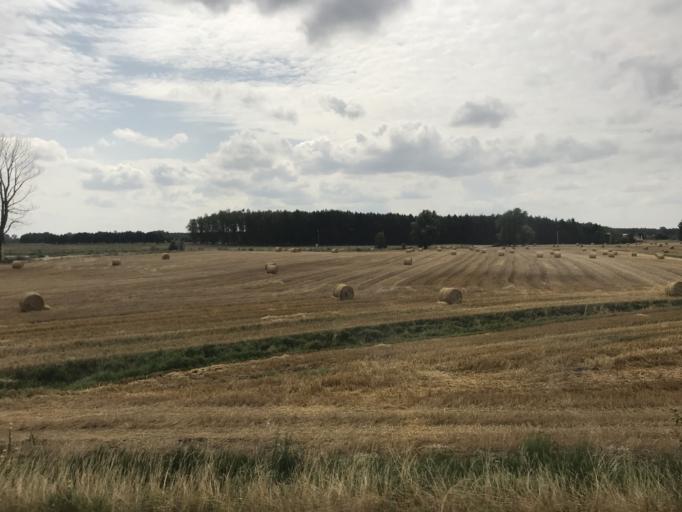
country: PL
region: Greater Poland Voivodeship
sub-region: Powiat gnieznienski
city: Trzemeszno
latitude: 52.5475
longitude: 17.7451
